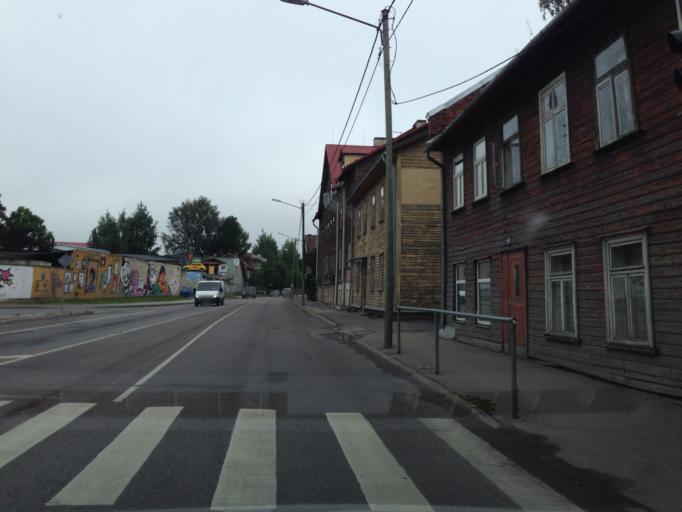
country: EE
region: Tartu
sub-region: Tartu linn
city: Tartu
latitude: 58.3664
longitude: 26.7214
